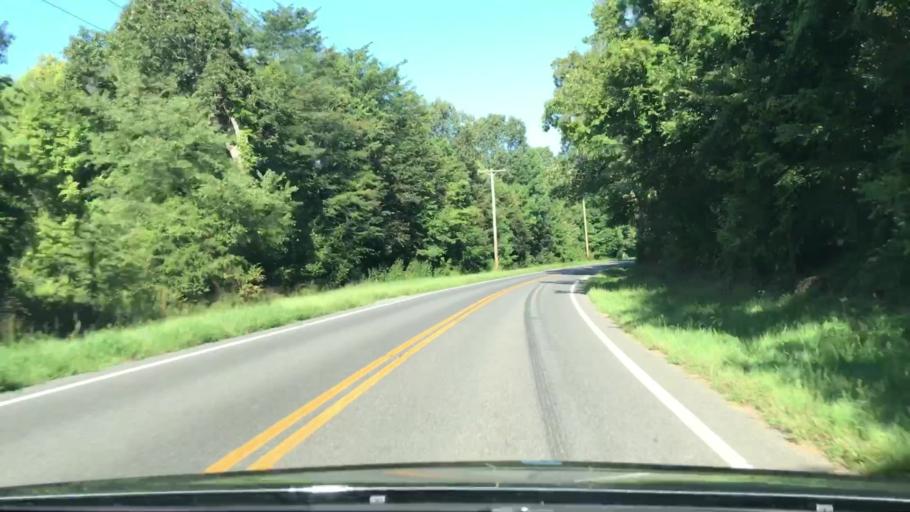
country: US
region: Kentucky
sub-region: Graves County
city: Mayfield
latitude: 36.7792
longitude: -88.5192
